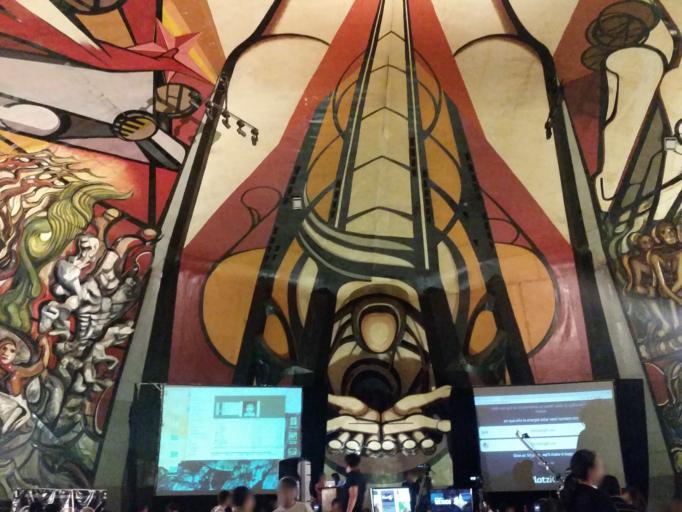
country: MX
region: Mexico City
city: Colonia del Valle
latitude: 19.3935
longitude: -99.1734
